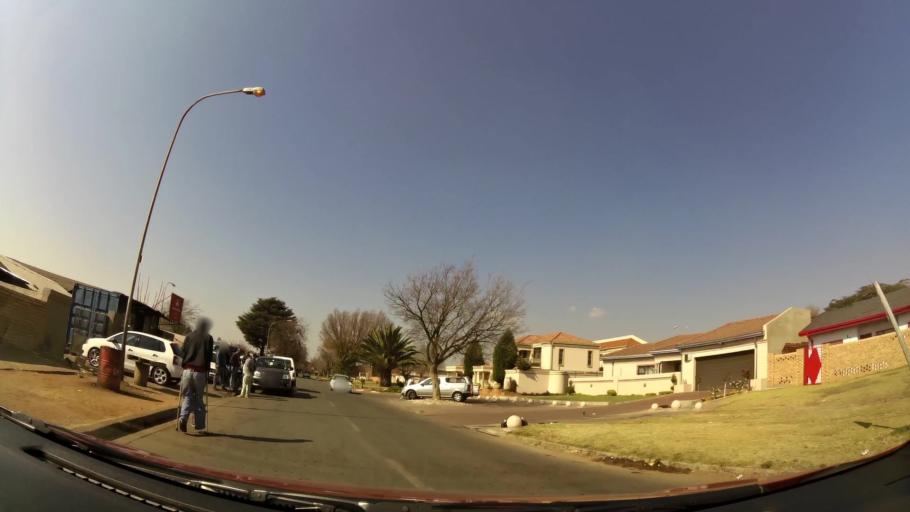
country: ZA
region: Gauteng
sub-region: City of Johannesburg Metropolitan Municipality
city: Johannesburg
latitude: -26.2451
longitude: 27.9581
